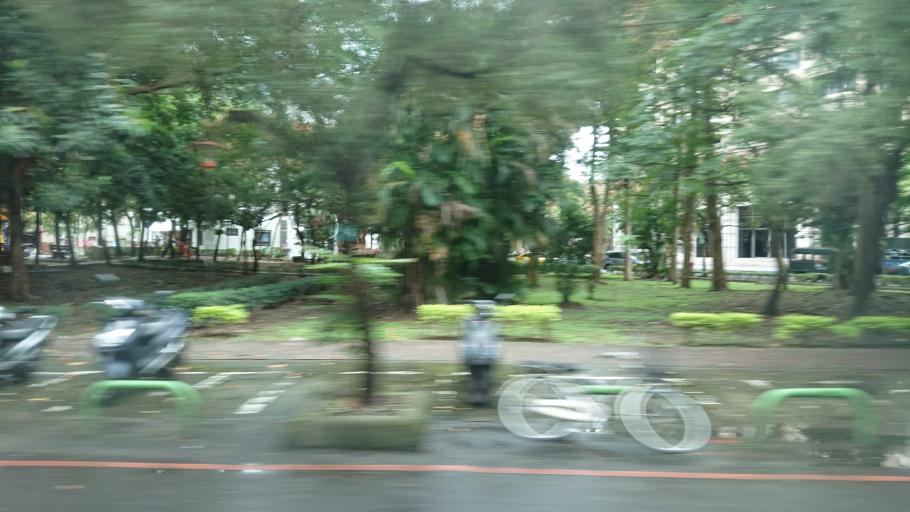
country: TW
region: Taipei
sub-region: Taipei
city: Banqiao
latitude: 24.9843
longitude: 121.4629
